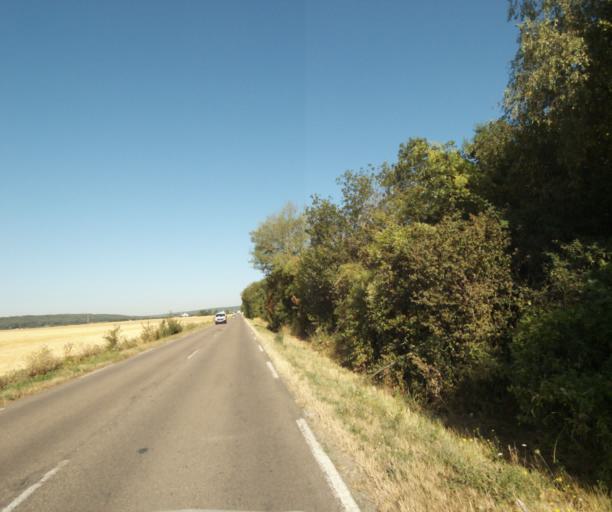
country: FR
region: Ile-de-France
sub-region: Departement de l'Essonne
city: Bouray-sur-Juine
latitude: 48.5147
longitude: 2.3165
